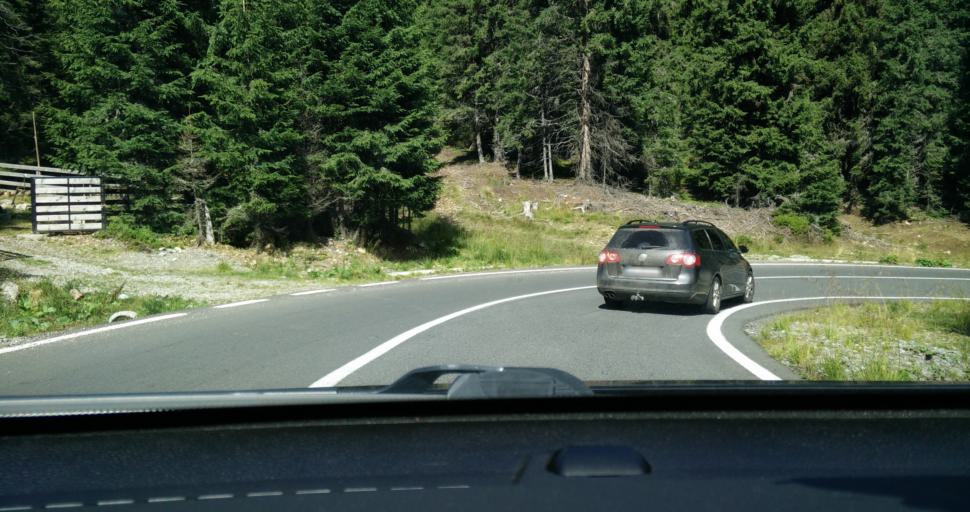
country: RO
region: Hunedoara
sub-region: Oras Petrila
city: Petrila
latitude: 45.4801
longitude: 23.6338
